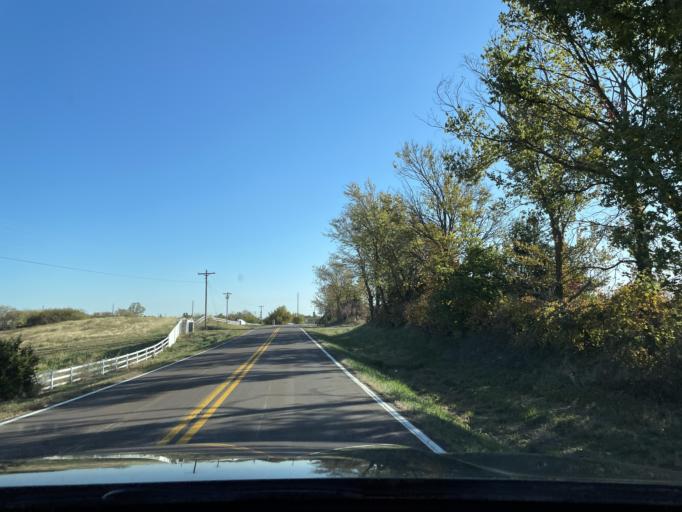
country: US
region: Missouri
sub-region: Andrew County
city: Savannah
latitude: 39.9211
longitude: -94.8653
